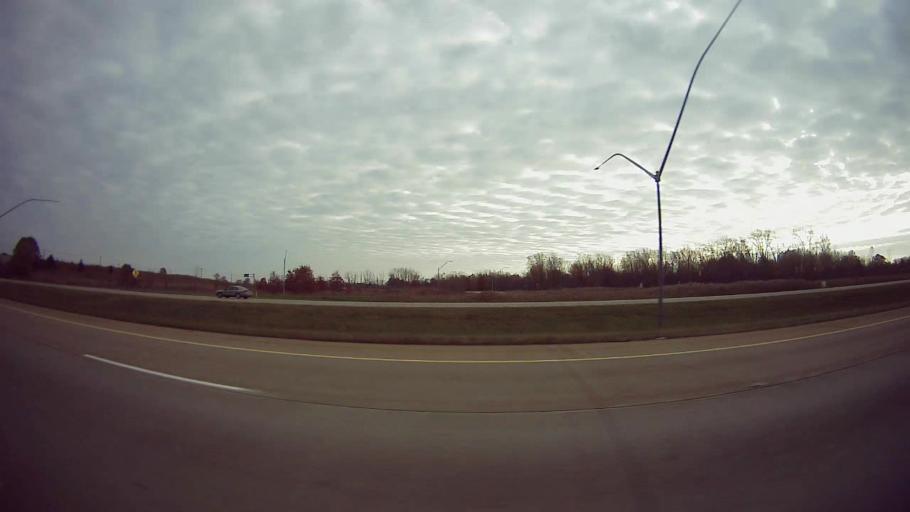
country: US
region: Michigan
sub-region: Wayne County
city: Romulus
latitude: 42.1891
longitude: -83.3888
